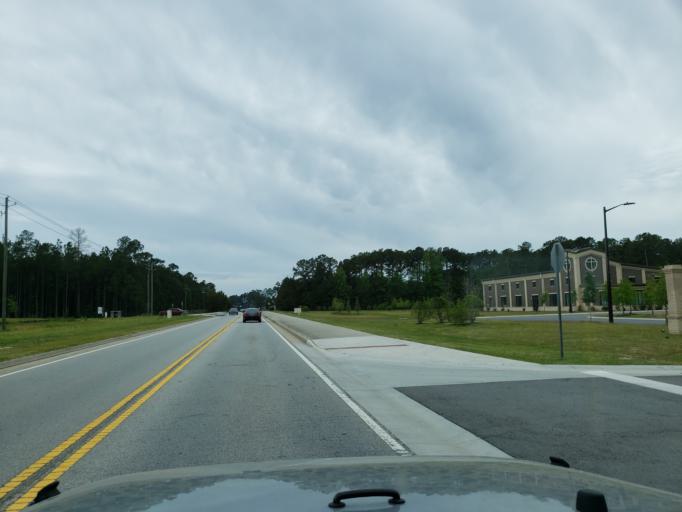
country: US
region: Georgia
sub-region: Chatham County
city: Pooler
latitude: 32.1565
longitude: -81.2378
